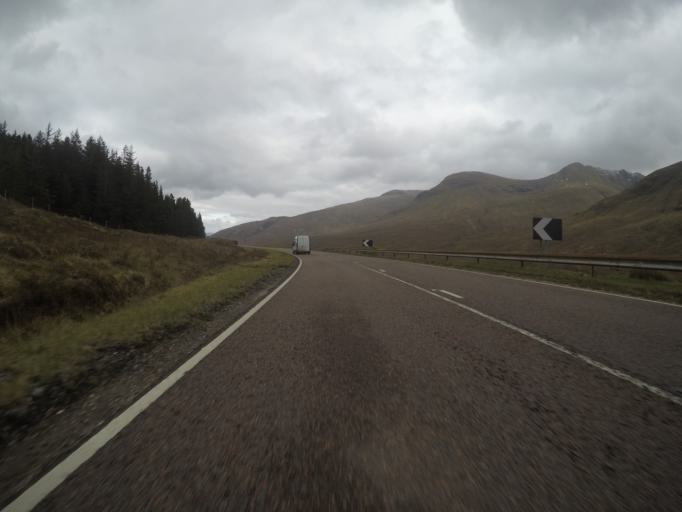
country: GB
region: Scotland
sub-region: Highland
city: Fort William
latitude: 57.1519
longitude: -5.2341
